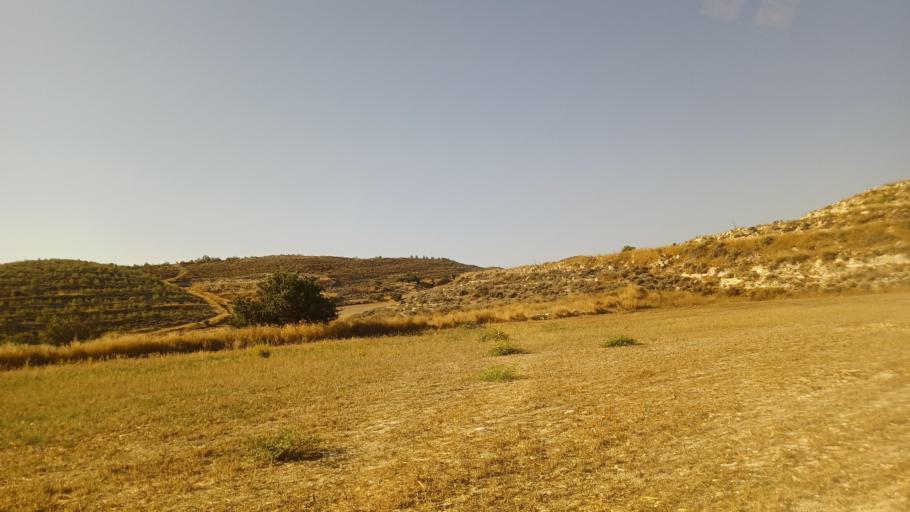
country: CY
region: Larnaka
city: Athienou
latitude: 35.0288
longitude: 33.5331
